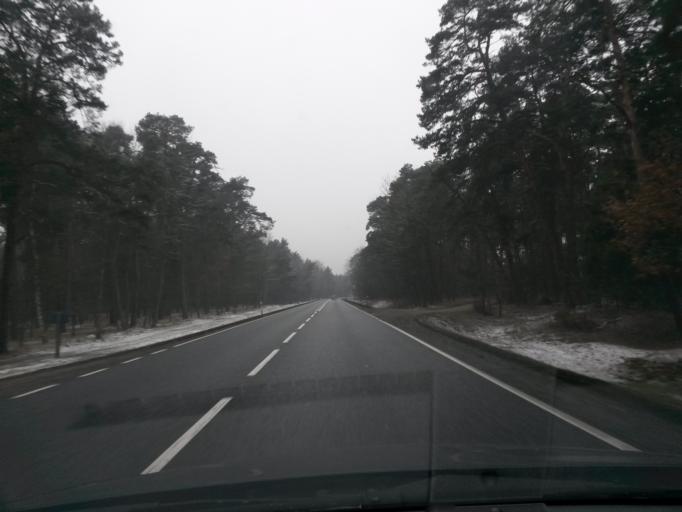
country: PL
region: Kujawsko-Pomorskie
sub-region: Powiat torunski
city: Wielka Nieszawka
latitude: 52.9770
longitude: 18.5154
